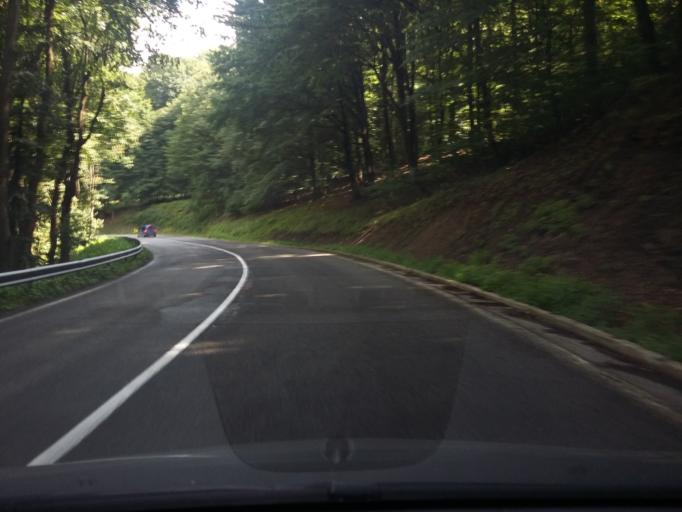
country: SK
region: Bratislavsky
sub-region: Okres Pezinok
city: Pezinok
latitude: 48.3608
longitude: 17.1764
